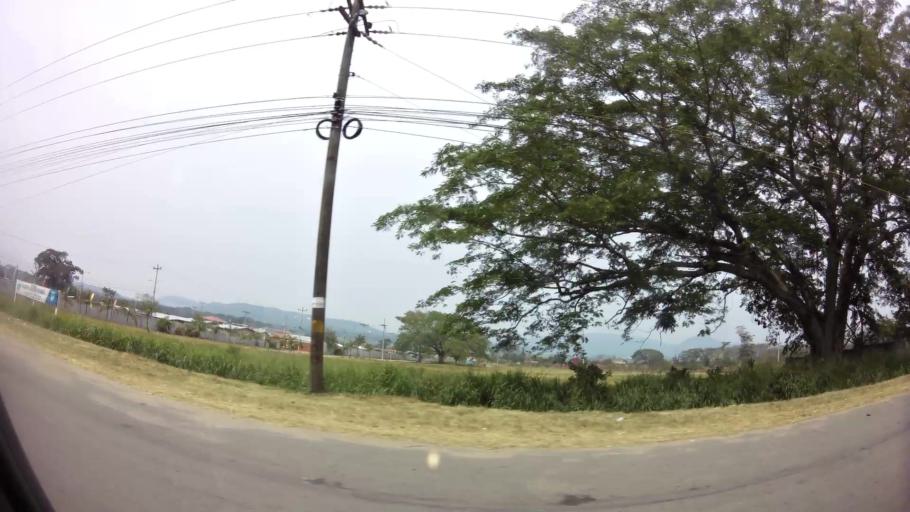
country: HN
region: Cortes
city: Villanueva
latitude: 15.3506
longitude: -87.9834
